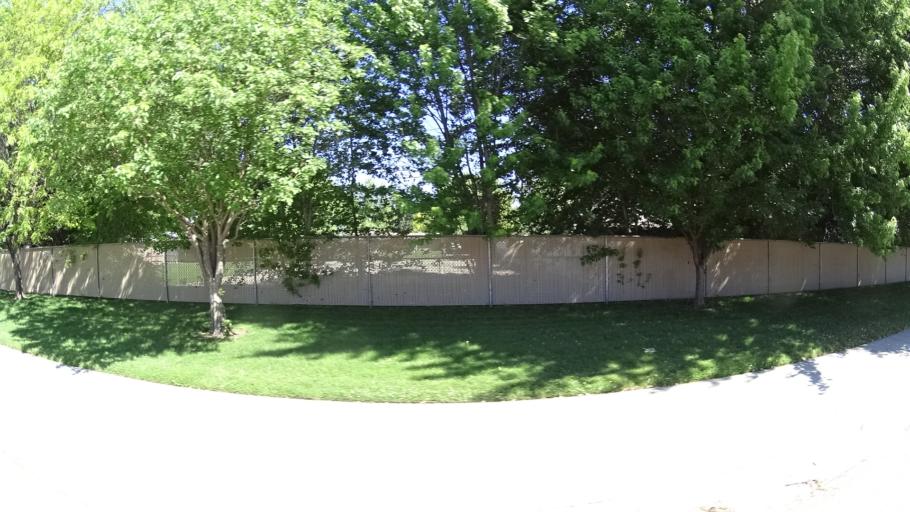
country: US
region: Idaho
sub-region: Ada County
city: Meridian
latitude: 43.6410
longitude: -116.3713
